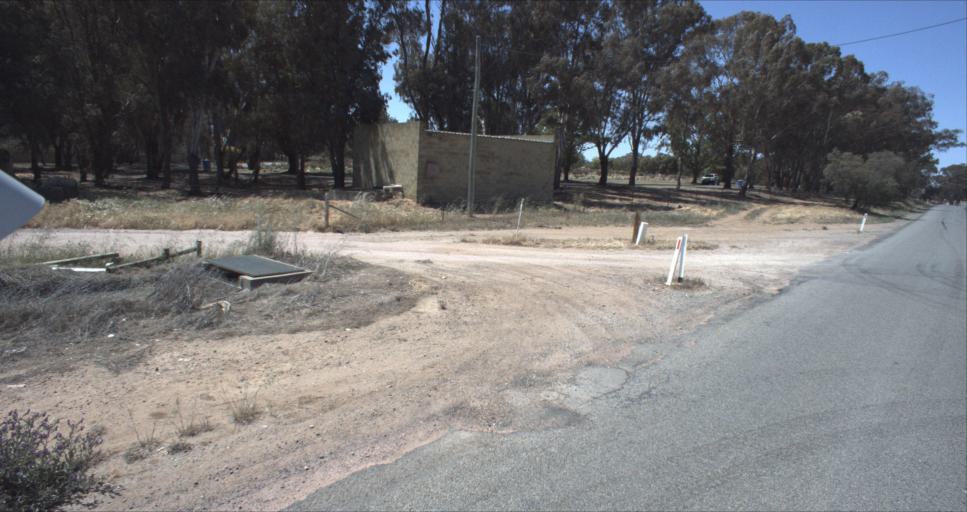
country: AU
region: New South Wales
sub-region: Leeton
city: Leeton
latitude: -34.5330
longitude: 146.3962
